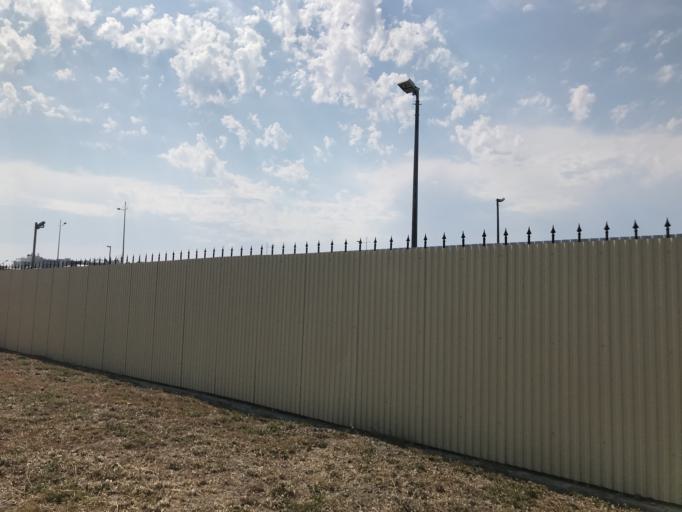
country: RU
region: Krasnodarskiy
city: Vysokoye
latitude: 43.3990
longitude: 39.9837
